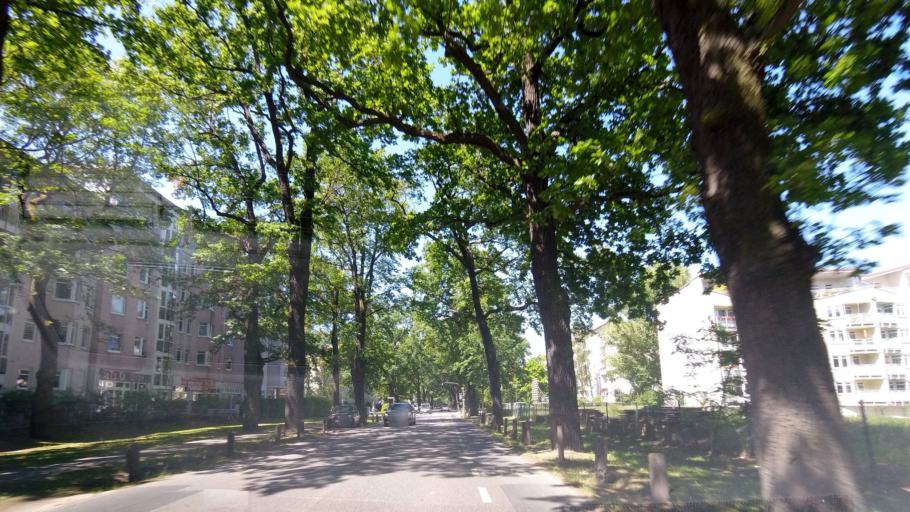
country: DE
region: Brandenburg
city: Potsdam
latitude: 52.3663
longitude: 13.1019
